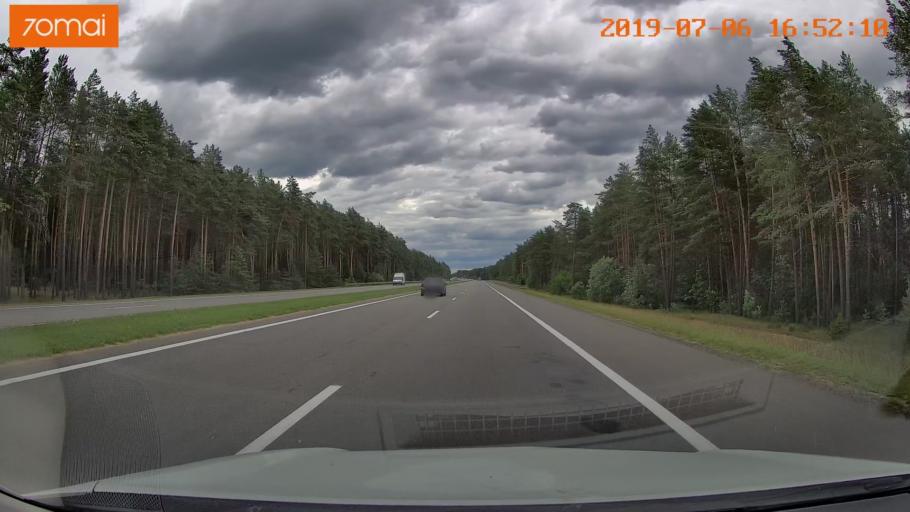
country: BY
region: Minsk
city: Rakaw
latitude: 53.9802
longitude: 27.0199
